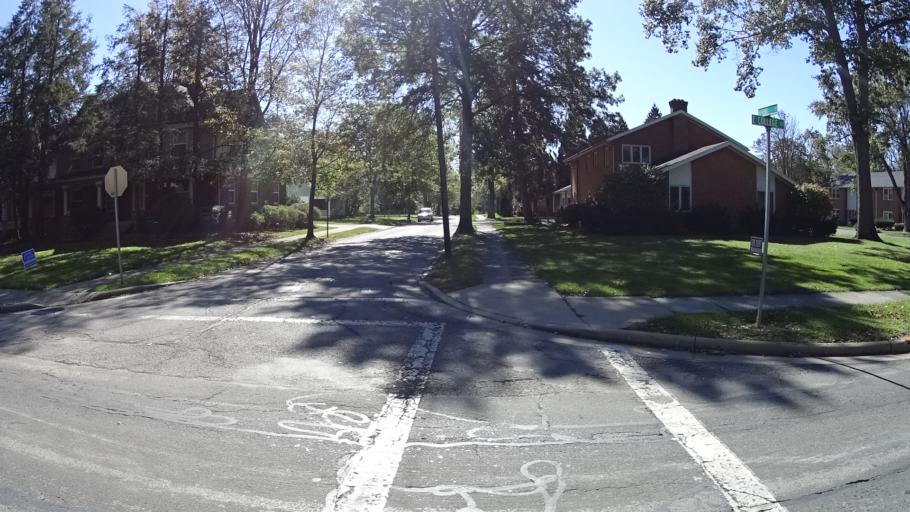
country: US
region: Ohio
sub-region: Lorain County
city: Oberlin
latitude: 41.2915
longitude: -82.2089
